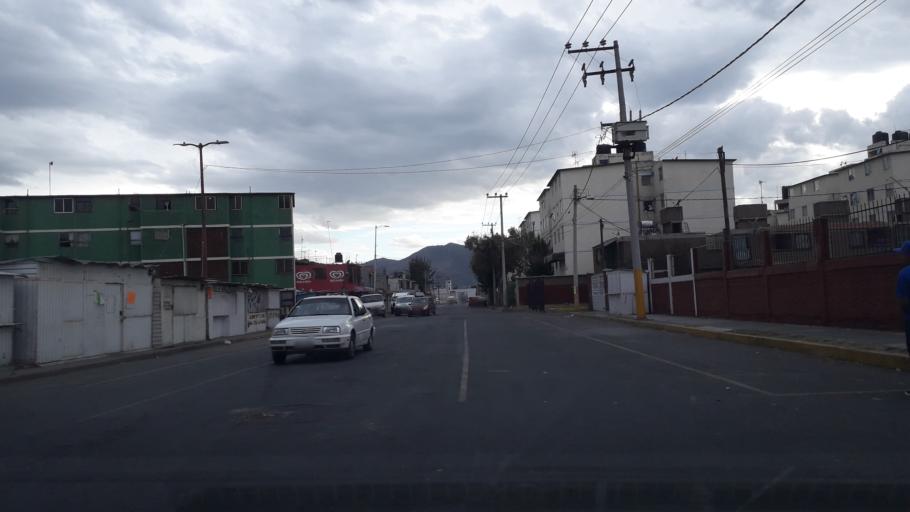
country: MX
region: Mexico
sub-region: Jaltenco
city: Alborada Jaltenco
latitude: 19.6642
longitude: -99.0706
